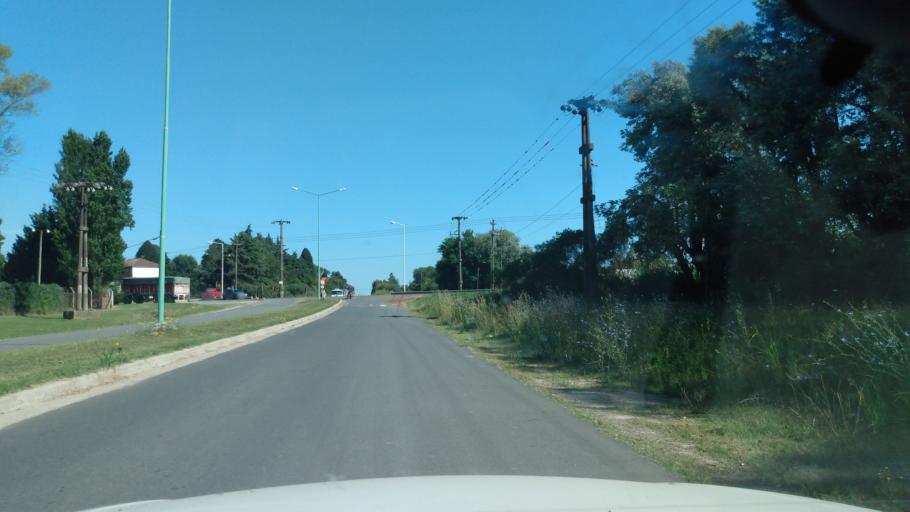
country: AR
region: Buenos Aires
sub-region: Partido de Lujan
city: Lujan
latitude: -34.5501
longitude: -59.1358
